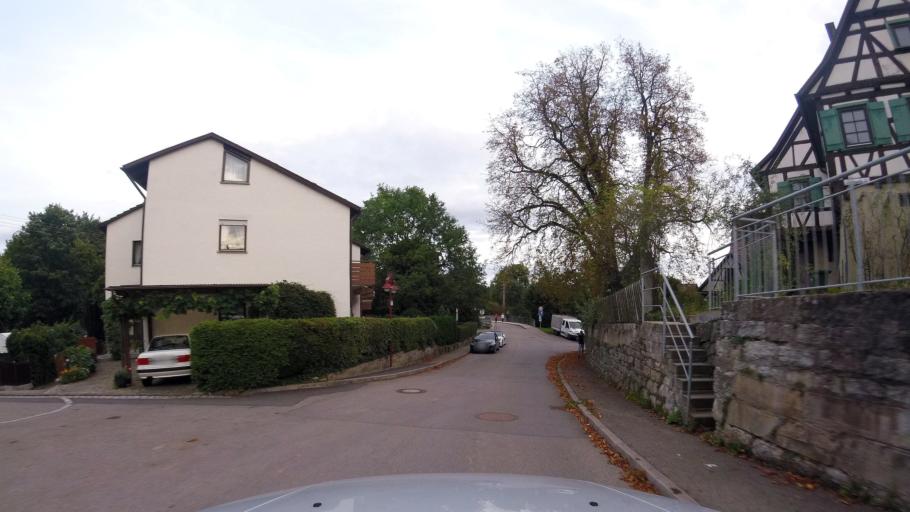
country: DE
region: Baden-Wuerttemberg
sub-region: Regierungsbezirk Stuttgart
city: Murr
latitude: 48.9632
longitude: 9.2620
